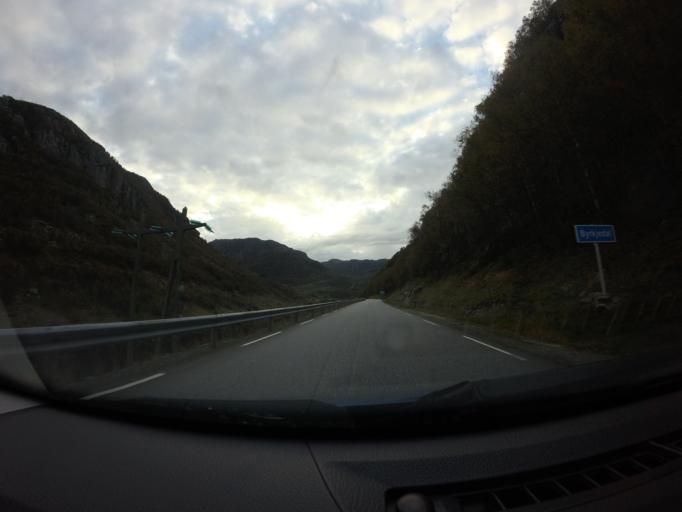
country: NO
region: Rogaland
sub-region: Forsand
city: Forsand
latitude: 58.7840
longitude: 6.2980
